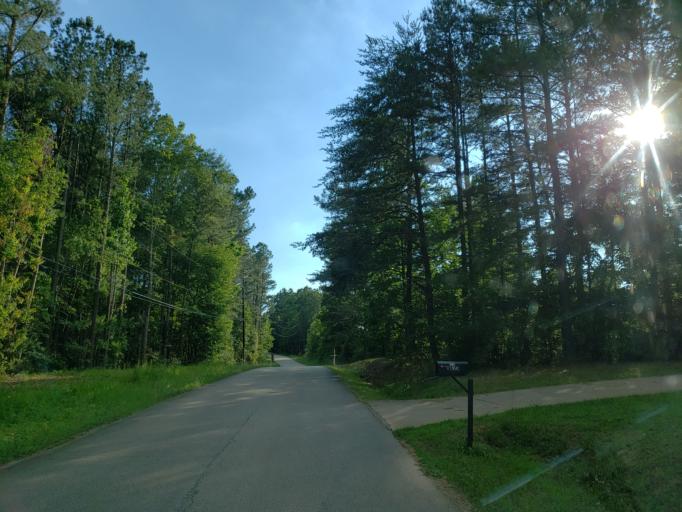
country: US
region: Georgia
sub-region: Haralson County
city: Buchanan
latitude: 33.9041
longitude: -85.2518
